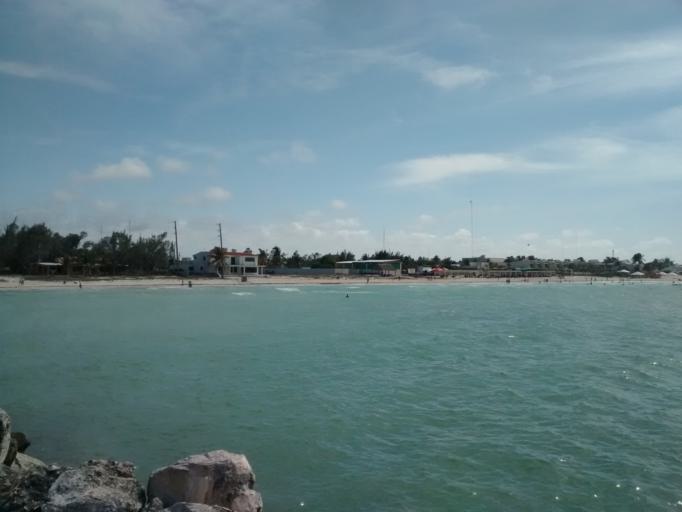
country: MX
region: Yucatan
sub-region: Progreso
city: Chelem
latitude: 21.2809
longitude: -89.7037
